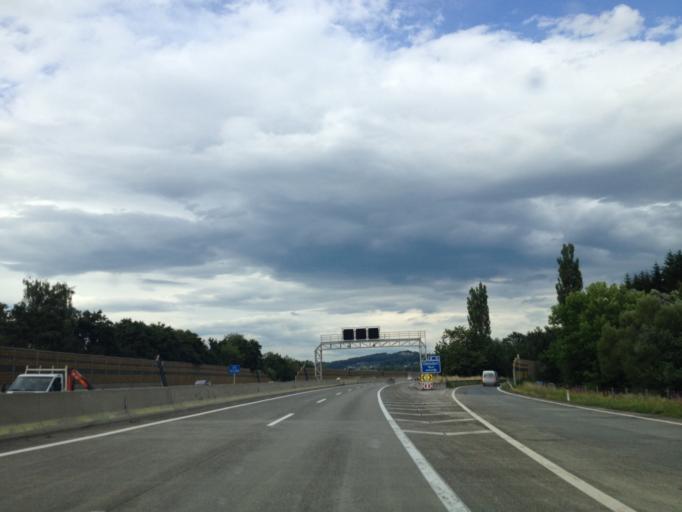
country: AT
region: Styria
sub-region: Politischer Bezirk Weiz
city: Ungerdorf
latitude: 47.0964
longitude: 15.6847
